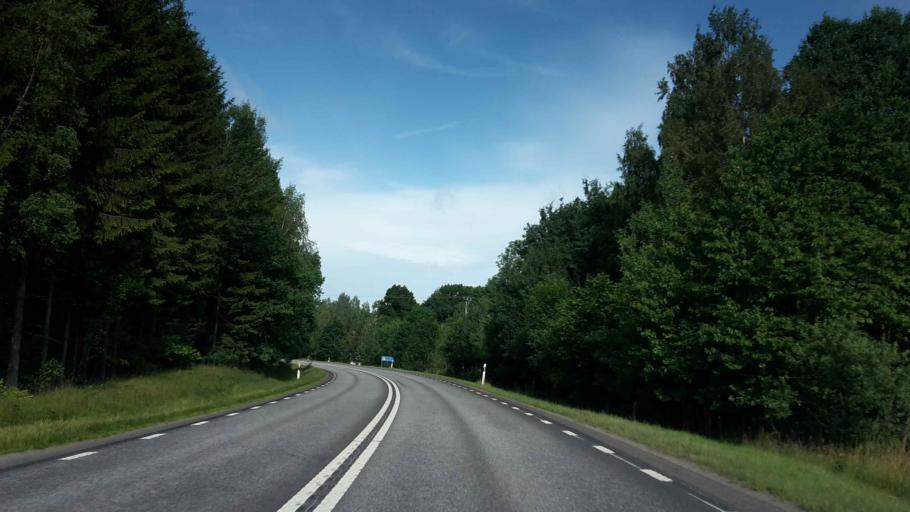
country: SE
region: OEstergoetland
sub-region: Motala Kommun
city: Borensberg
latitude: 58.5369
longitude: 15.3805
